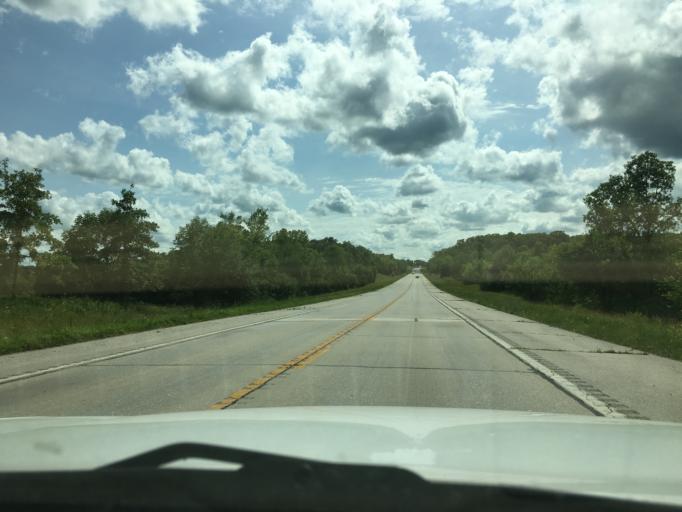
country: US
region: Missouri
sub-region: Franklin County
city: Gerald
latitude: 38.4166
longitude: -91.2976
